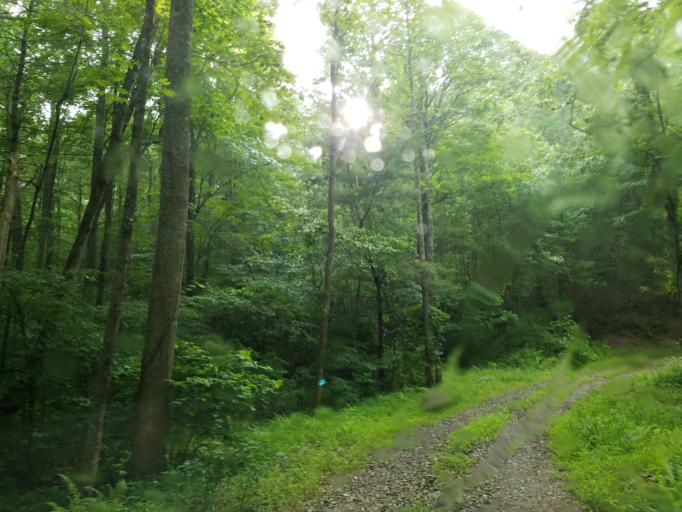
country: US
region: Georgia
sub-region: Fannin County
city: Blue Ridge
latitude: 34.7207
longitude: -84.2014
